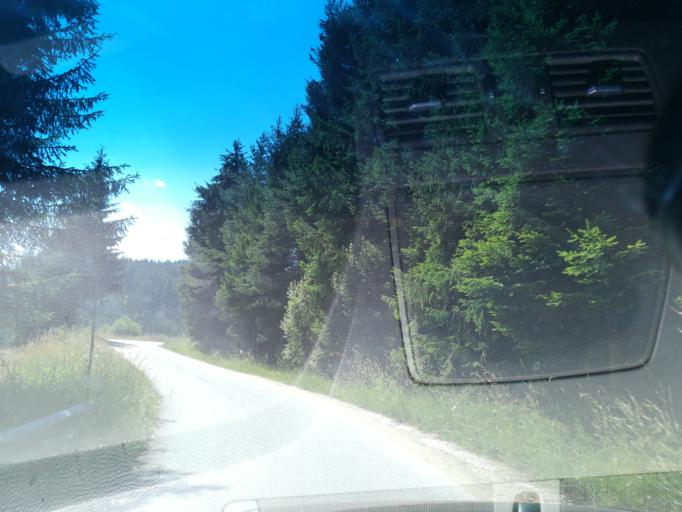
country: BG
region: Smolyan
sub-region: Obshtina Chepelare
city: Chepelare
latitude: 41.6719
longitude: 24.7902
